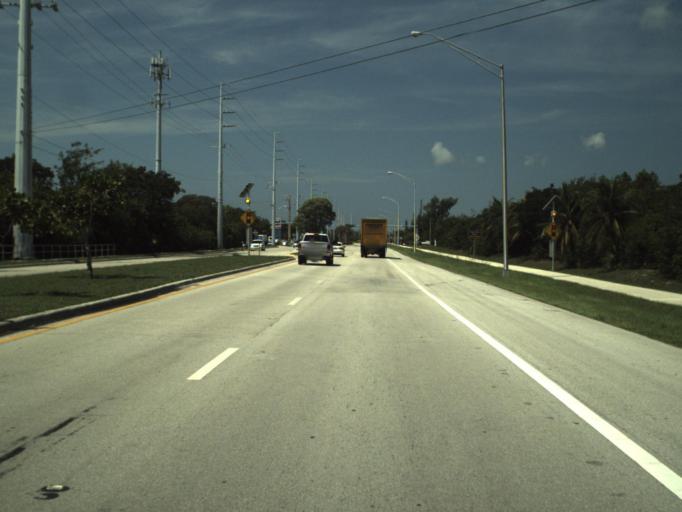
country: US
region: Florida
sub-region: Monroe County
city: Marathon
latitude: 24.7358
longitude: -81.0111
